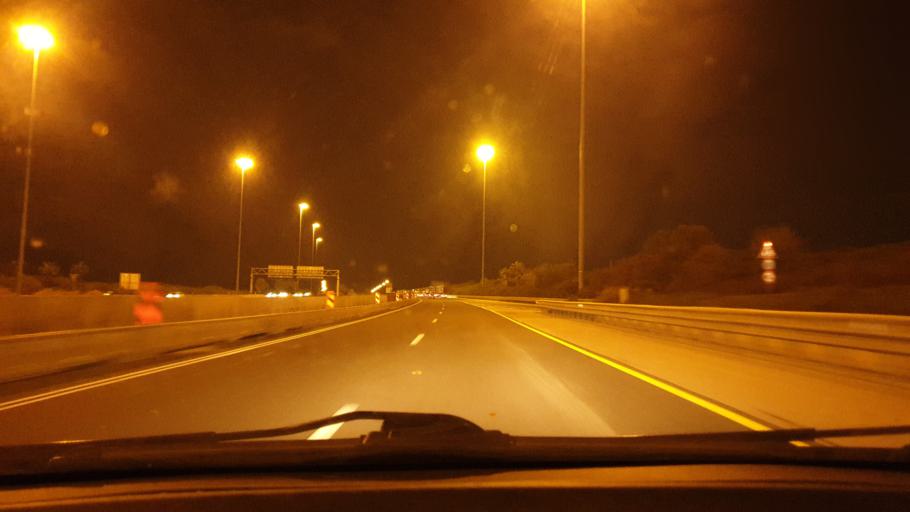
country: IL
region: Central District
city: Ramla
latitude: 31.9175
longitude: 34.8617
